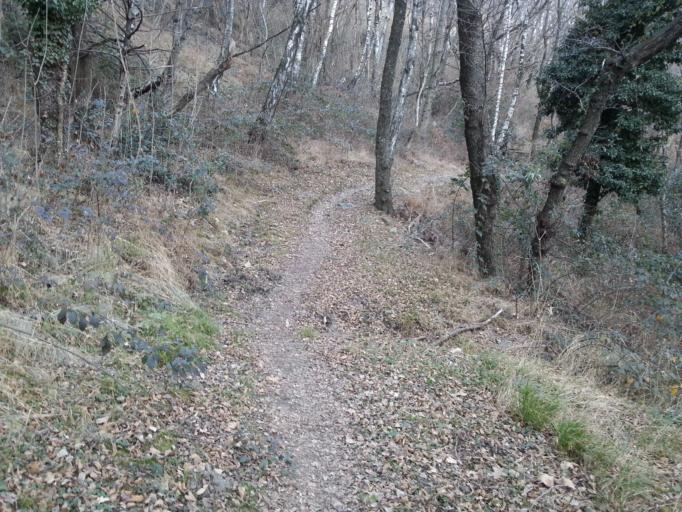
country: CH
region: Ticino
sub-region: Bellinzona District
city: Cadenazzo
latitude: 46.1362
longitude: 8.9178
